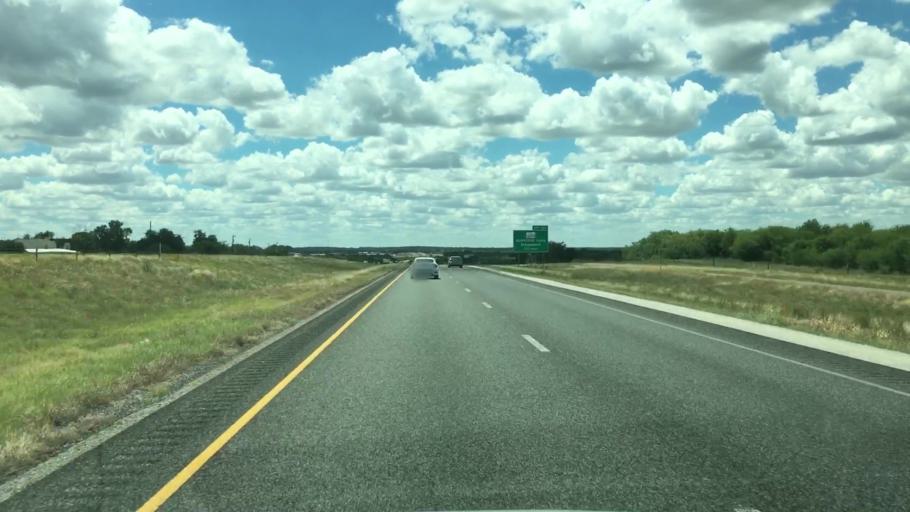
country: US
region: Texas
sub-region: Bexar County
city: Elmendorf
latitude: 29.2435
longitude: -98.3984
